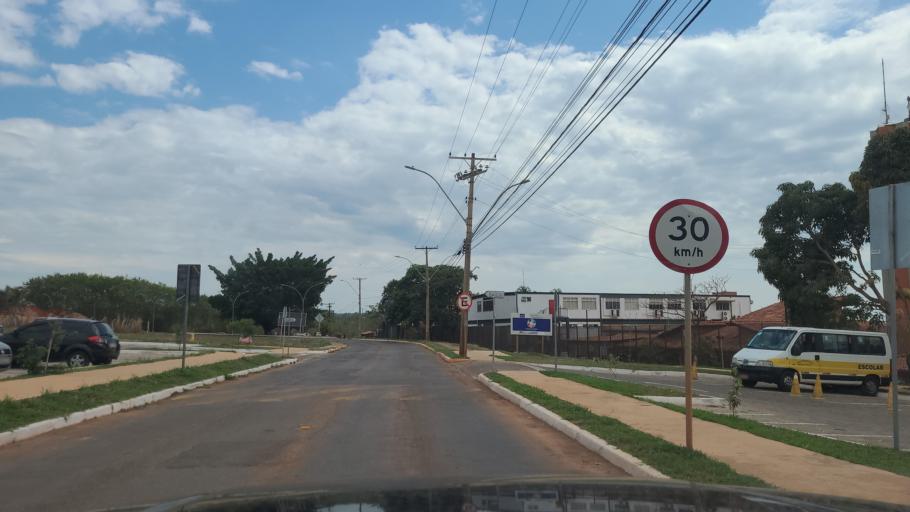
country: BR
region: Federal District
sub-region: Brasilia
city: Brasilia
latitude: -15.8537
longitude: -47.8501
